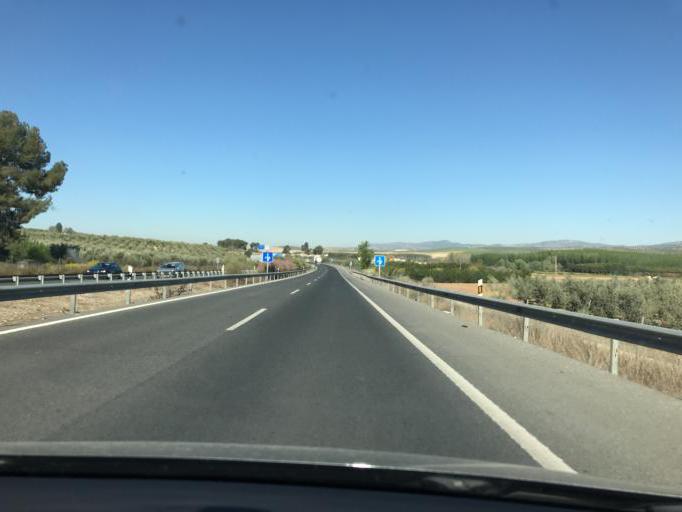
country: ES
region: Andalusia
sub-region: Provincia de Granada
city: Lachar
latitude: 37.1946
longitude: -3.8599
